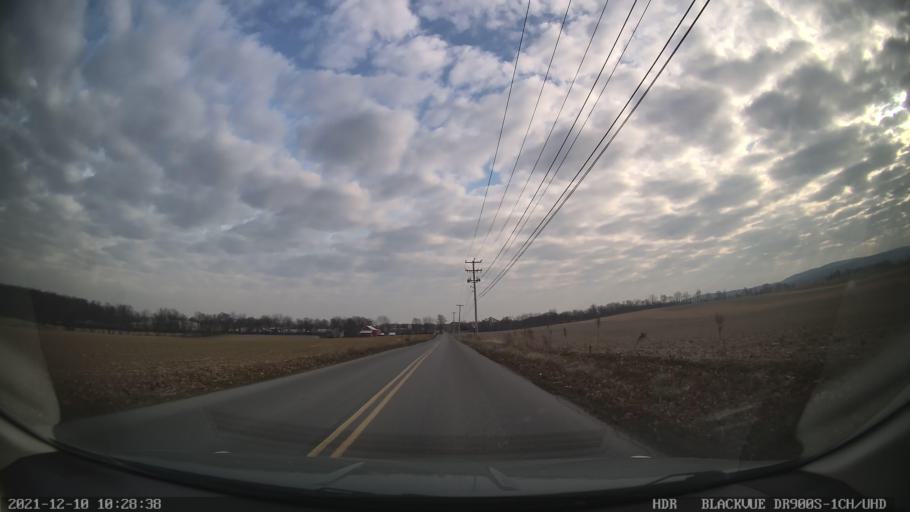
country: US
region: Pennsylvania
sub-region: Berks County
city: Kutztown
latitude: 40.5127
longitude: -75.7390
